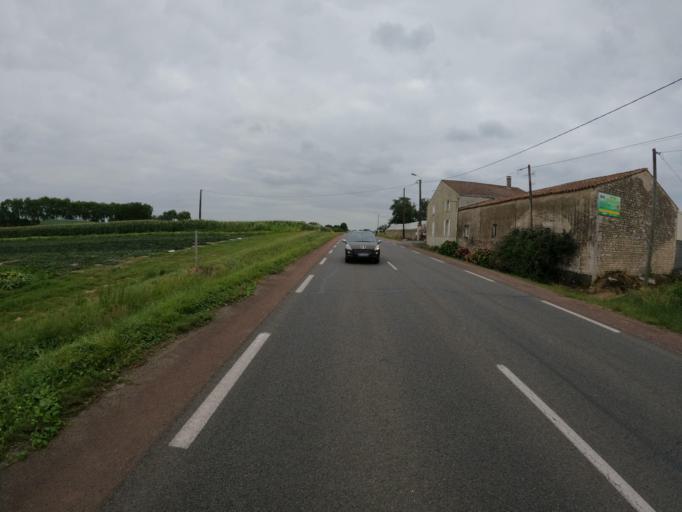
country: FR
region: Pays de la Loire
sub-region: Departement de la Vendee
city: Saint-Hilaire-des-Loges
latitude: 46.4092
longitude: -0.6846
